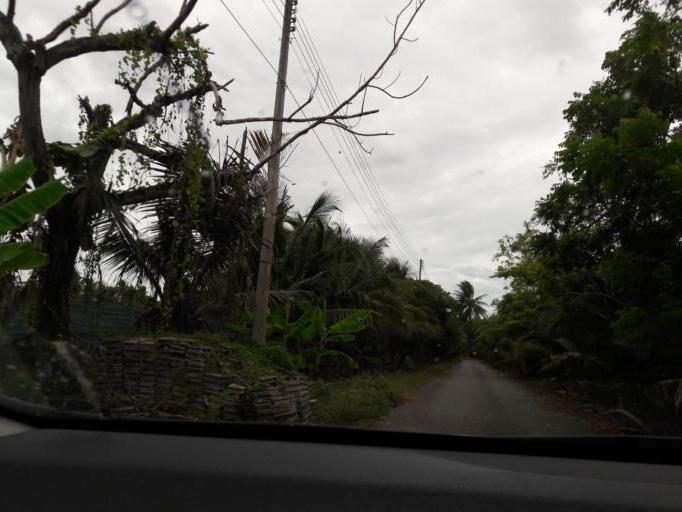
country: TH
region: Ratchaburi
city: Damnoen Saduak
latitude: 13.5461
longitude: 100.0296
